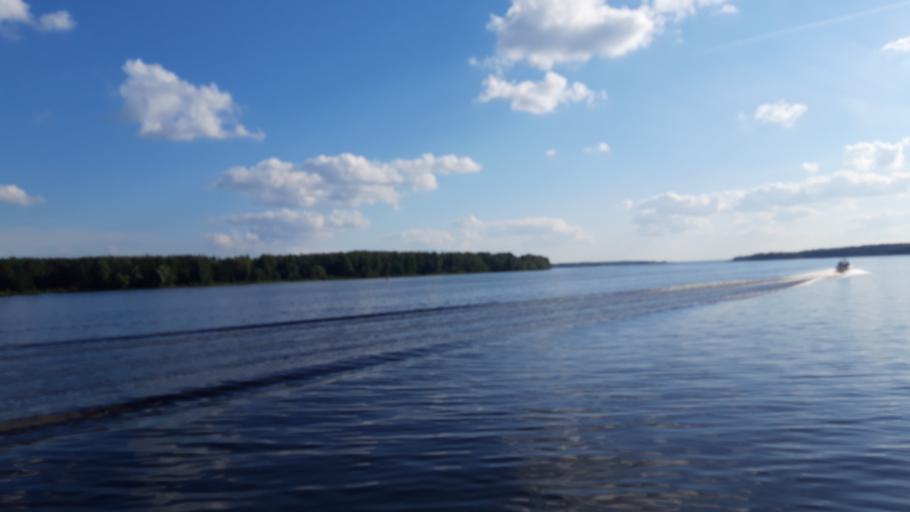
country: RU
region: Tverskaya
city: Konakovo
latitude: 56.6996
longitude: 36.7082
